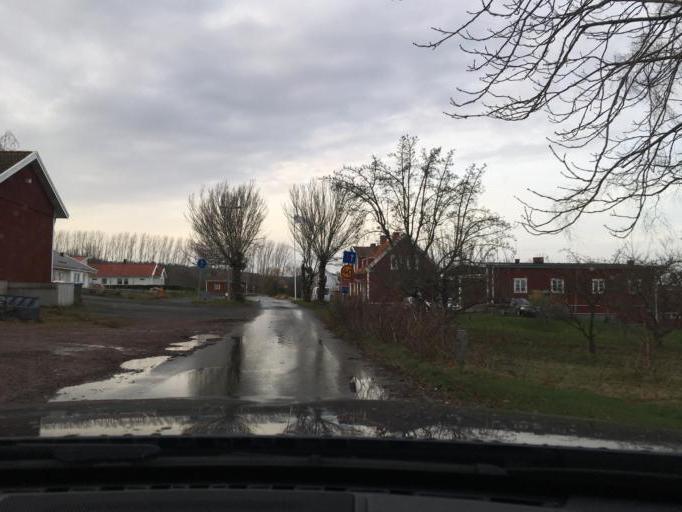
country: SE
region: Joenkoeping
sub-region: Jonkopings Kommun
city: Graenna
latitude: 58.0129
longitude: 14.4525
